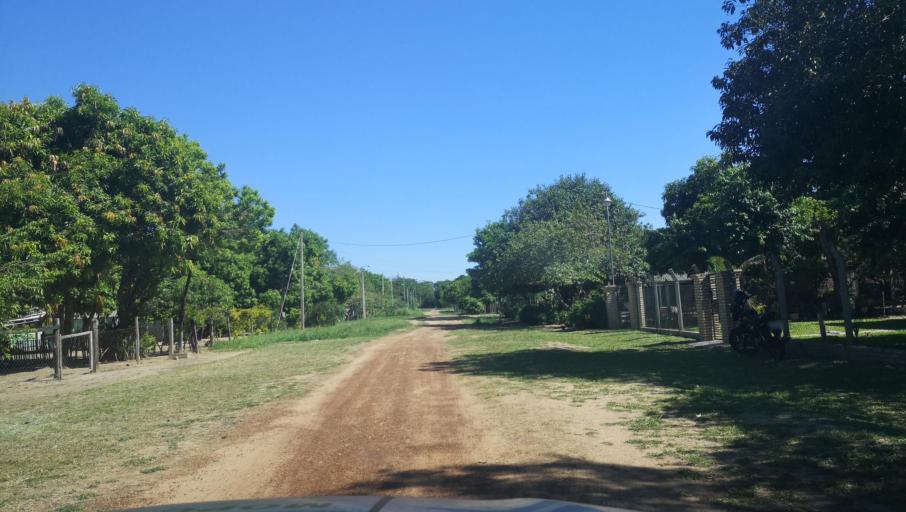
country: PY
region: Caaguazu
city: Carayao
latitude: -25.1989
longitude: -56.3937
